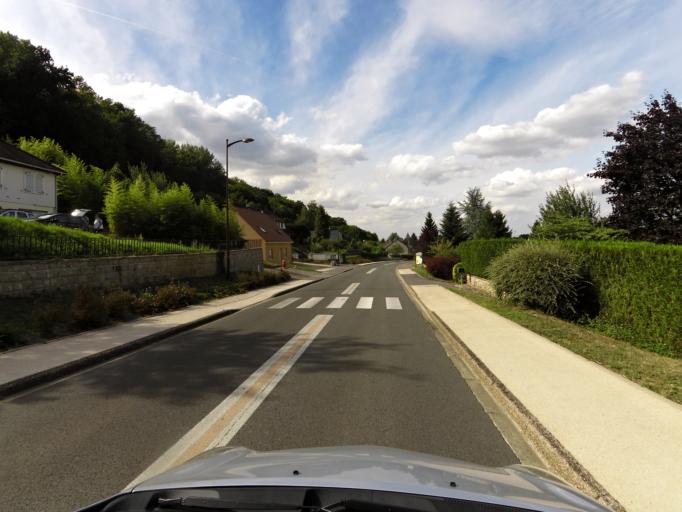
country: FR
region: Picardie
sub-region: Departement de l'Aisne
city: Bruyeres-et-Montberault
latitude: 49.5182
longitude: 3.6669
